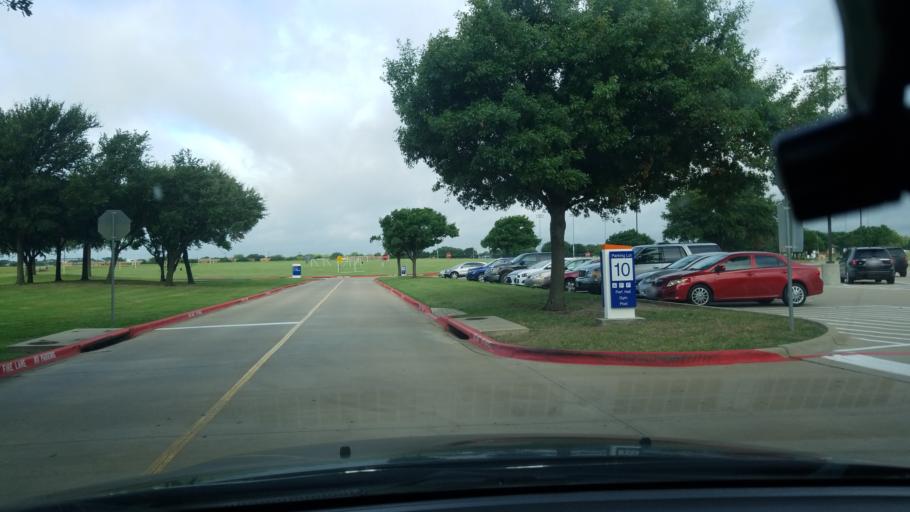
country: US
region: Texas
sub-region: Dallas County
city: Mesquite
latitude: 32.8132
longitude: -96.6600
